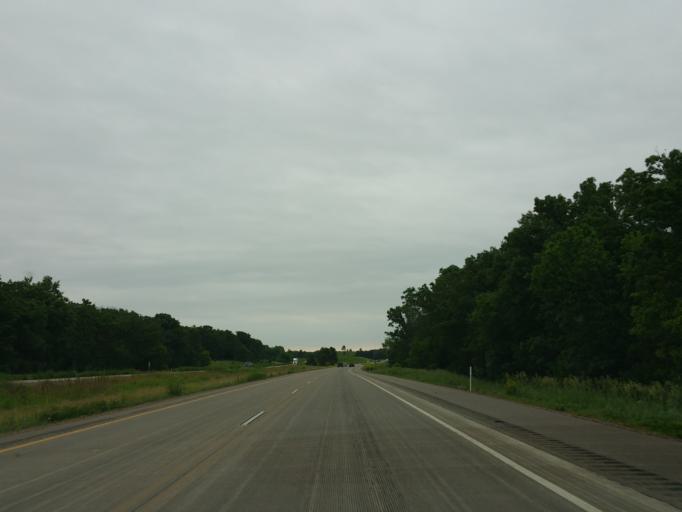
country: US
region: Wisconsin
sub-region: Eau Claire County
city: Fall Creek
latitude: 44.6777
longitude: -91.3253
